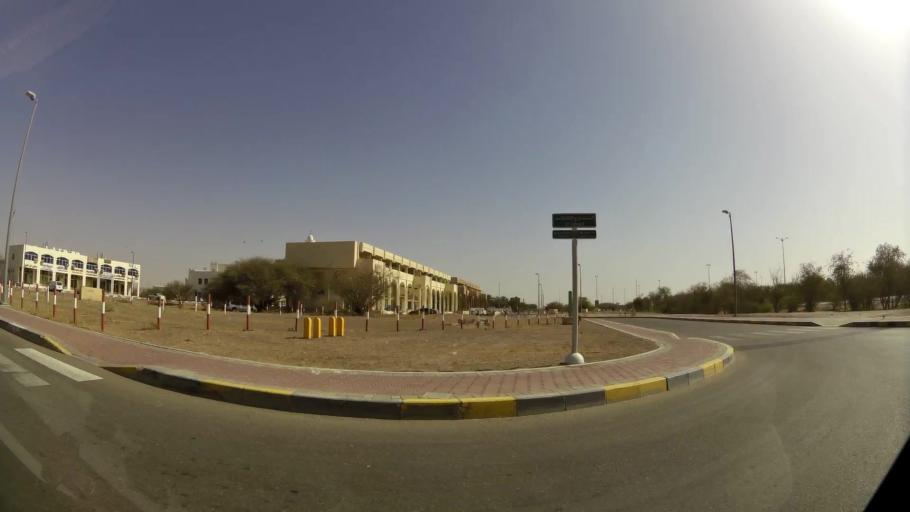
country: OM
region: Al Buraimi
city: Al Buraymi
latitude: 24.3375
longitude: 55.8042
